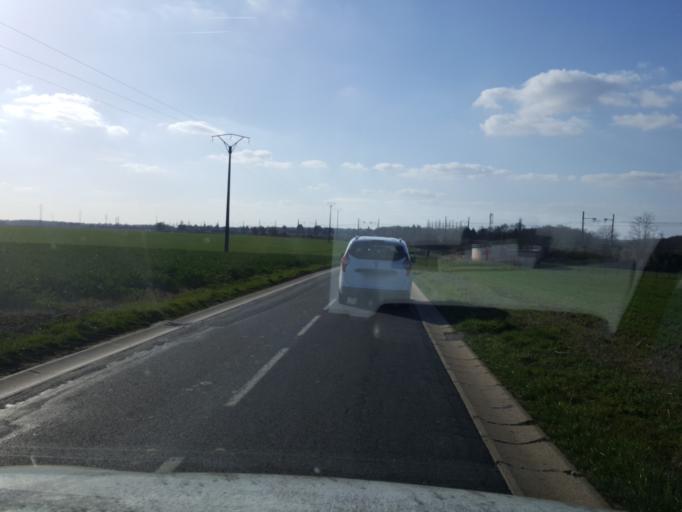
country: FR
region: Ile-de-France
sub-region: Departement des Yvelines
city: Gazeran
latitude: 48.6265
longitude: 1.7913
